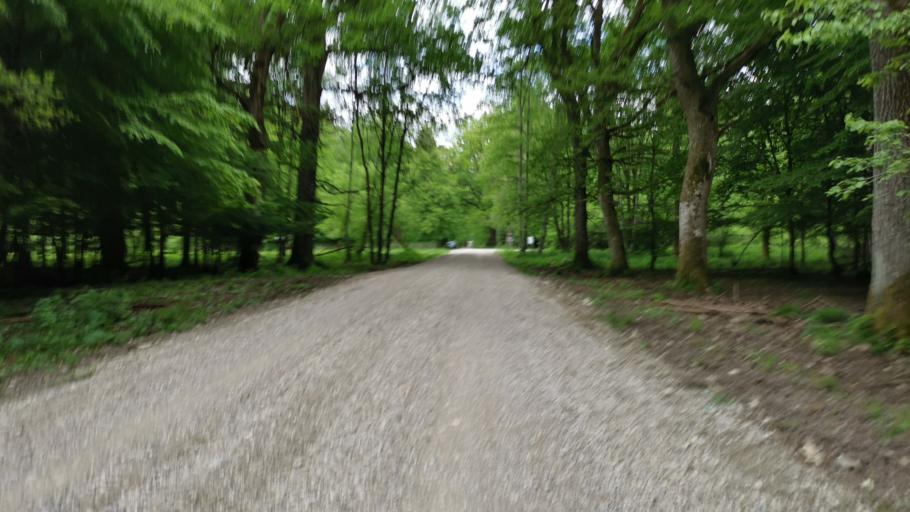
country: DE
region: Bavaria
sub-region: Upper Bavaria
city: Baierbrunn
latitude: 48.0456
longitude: 11.4725
